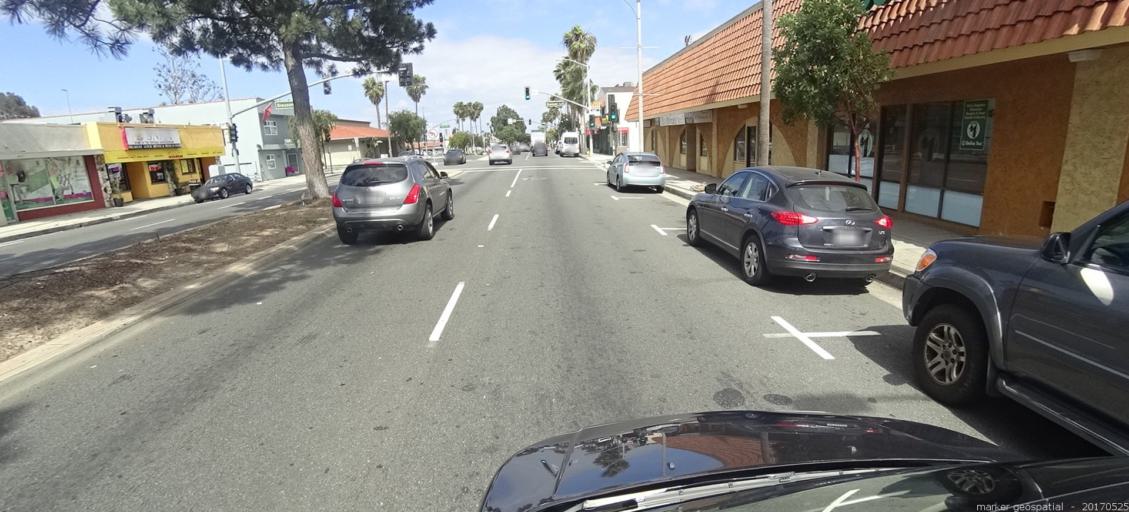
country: US
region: California
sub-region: Los Angeles County
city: Lawndale
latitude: 33.8728
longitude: -118.3712
